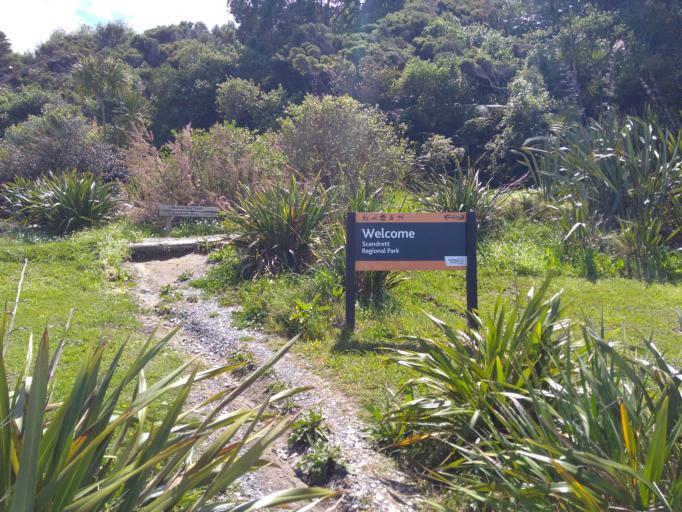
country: NZ
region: Auckland
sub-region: Auckland
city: Warkworth
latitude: -36.4455
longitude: 174.7668
